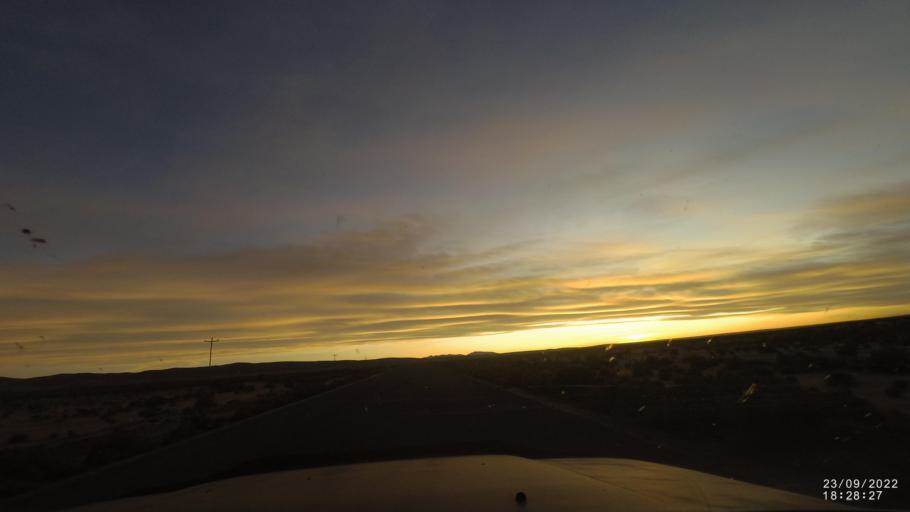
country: BO
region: Oruro
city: Challapata
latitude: -19.3375
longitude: -67.1774
